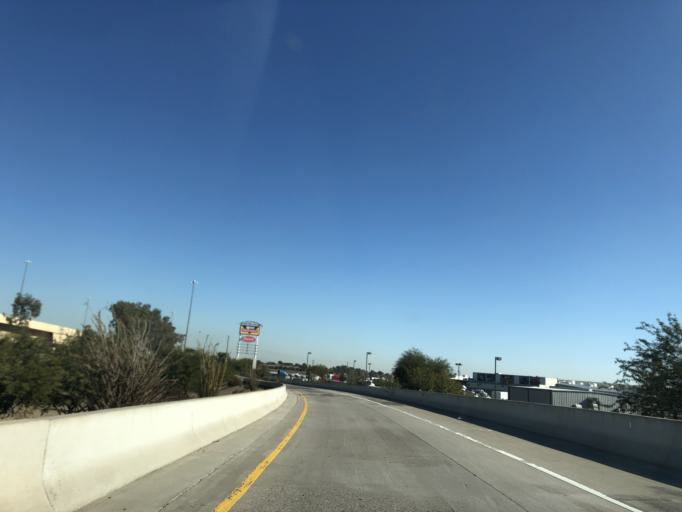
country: US
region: Arizona
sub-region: Maricopa County
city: Tolleson
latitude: 33.4609
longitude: -112.2680
